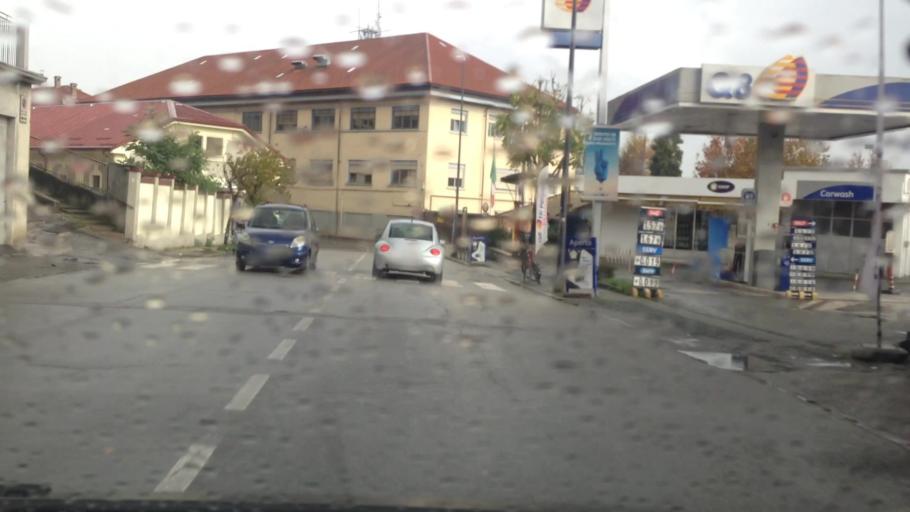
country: IT
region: Piedmont
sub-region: Provincia di Asti
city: Asti
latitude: 44.9033
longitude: 8.2085
